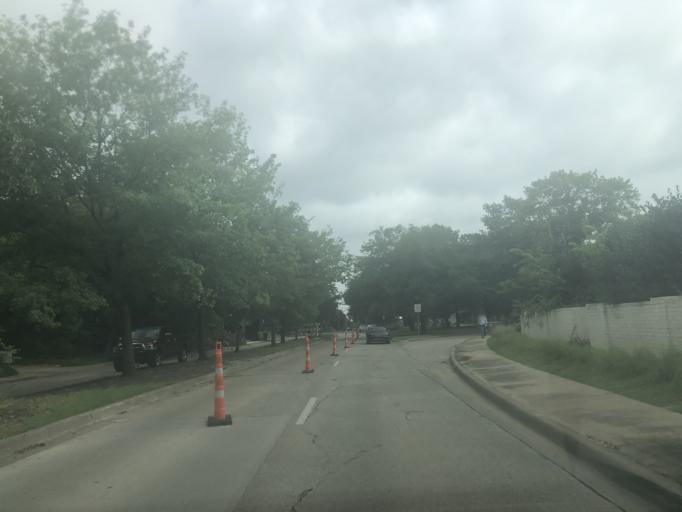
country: US
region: Texas
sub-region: Dallas County
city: University Park
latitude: 32.8545
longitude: -96.8367
